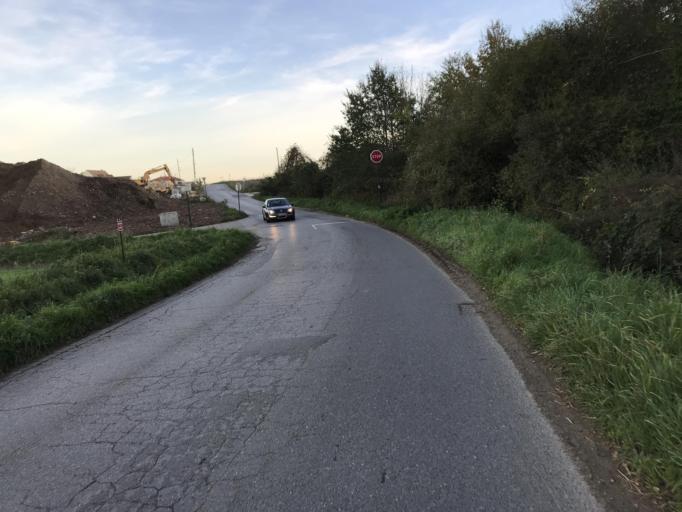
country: FR
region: Ile-de-France
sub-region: Departement de l'Essonne
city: Saulx-les-Chartreux
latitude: 48.6874
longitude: 2.2533
